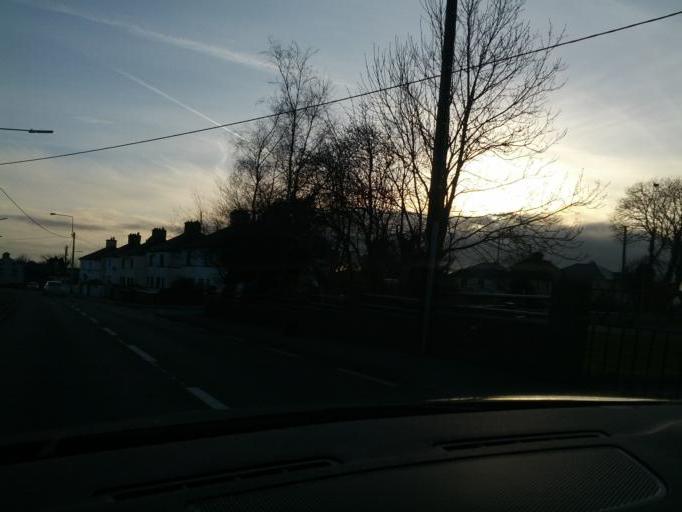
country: IE
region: Connaught
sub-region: Sligo
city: Tobercurry
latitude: 54.0566
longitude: -8.7260
